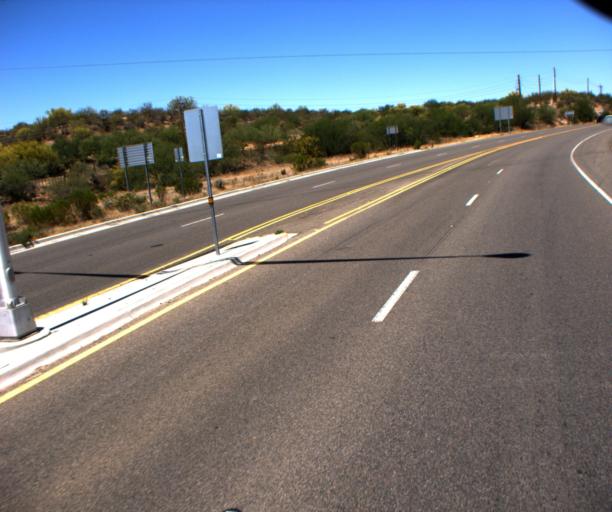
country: US
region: Arizona
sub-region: Maricopa County
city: Wickenburg
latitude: 33.9858
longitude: -112.7400
